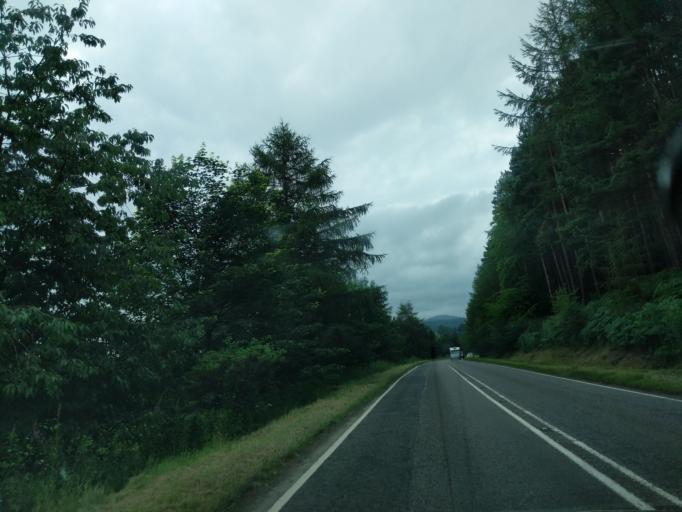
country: GB
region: Scotland
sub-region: Moray
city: Rothes
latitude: 57.4970
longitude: -3.1903
